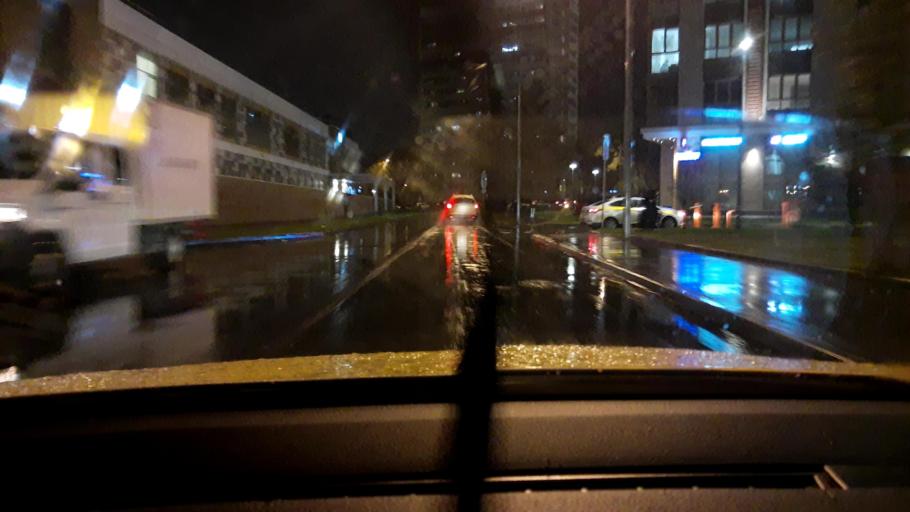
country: RU
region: Moscow
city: Sviblovo
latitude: 55.8481
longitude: 37.6343
